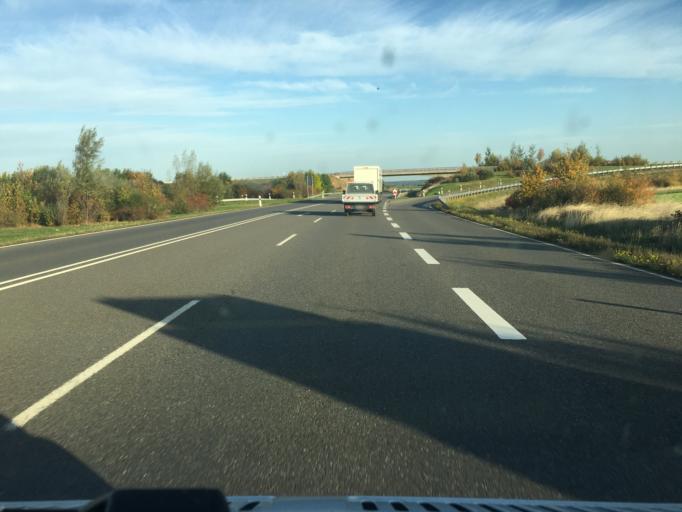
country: DE
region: Saxony
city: Lichtentanne
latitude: 50.6681
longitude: 12.4435
